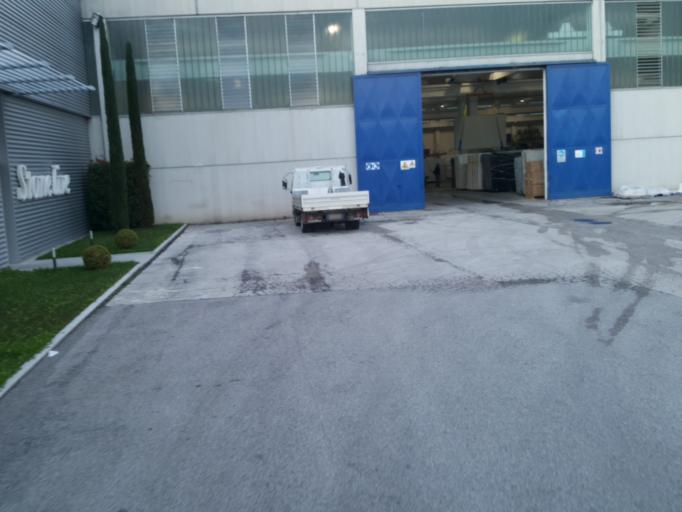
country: IT
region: Veneto
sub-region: Provincia di Verona
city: Volargne
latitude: 45.5314
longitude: 10.8163
